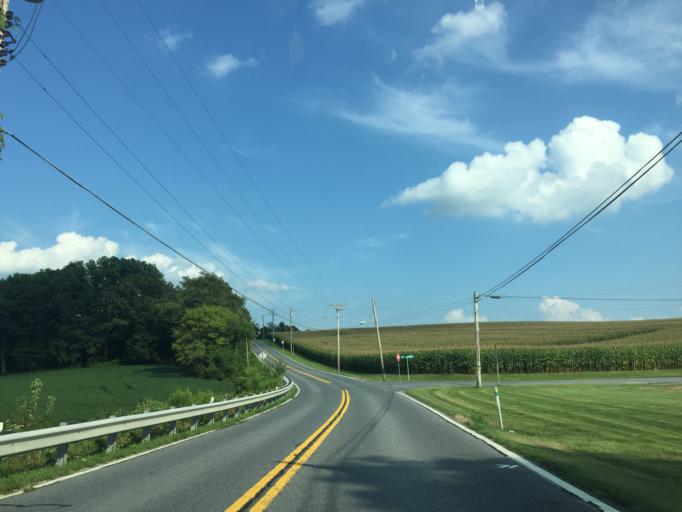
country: US
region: Maryland
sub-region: Carroll County
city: Hampstead
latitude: 39.5940
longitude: -76.7515
